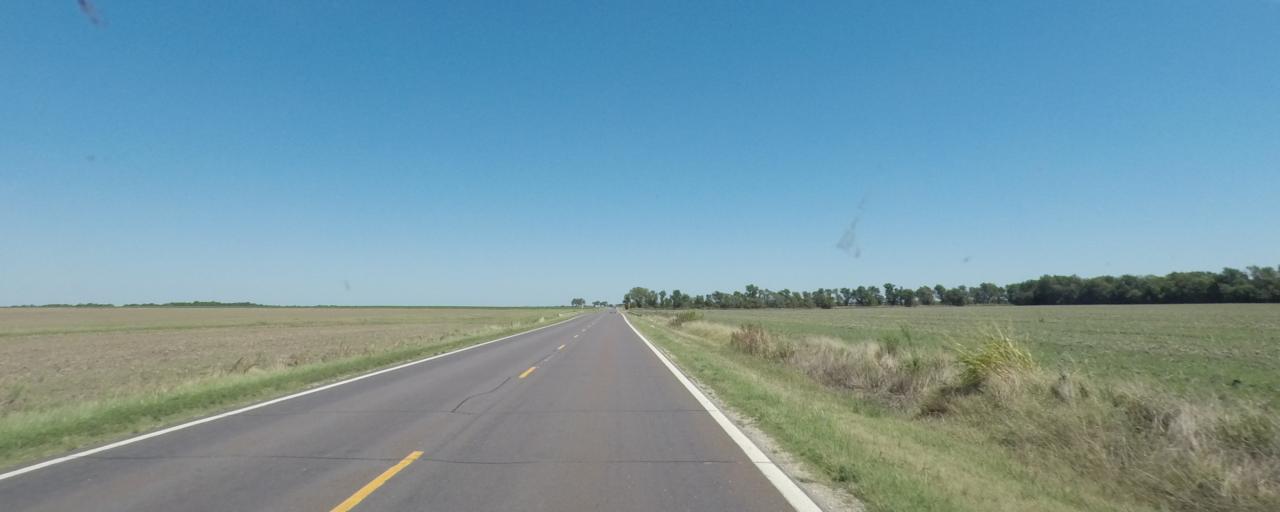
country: US
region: Kansas
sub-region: Sumner County
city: Wellington
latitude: 37.1623
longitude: -97.4022
